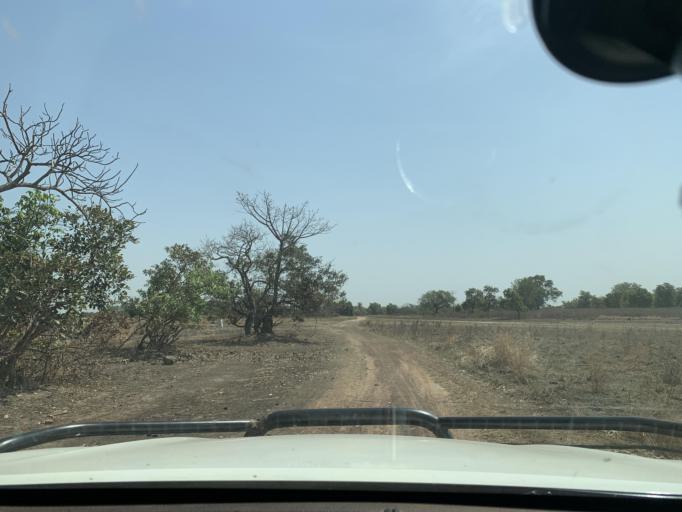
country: ML
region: Sikasso
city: Kolondieba
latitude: 10.8413
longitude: -6.8028
